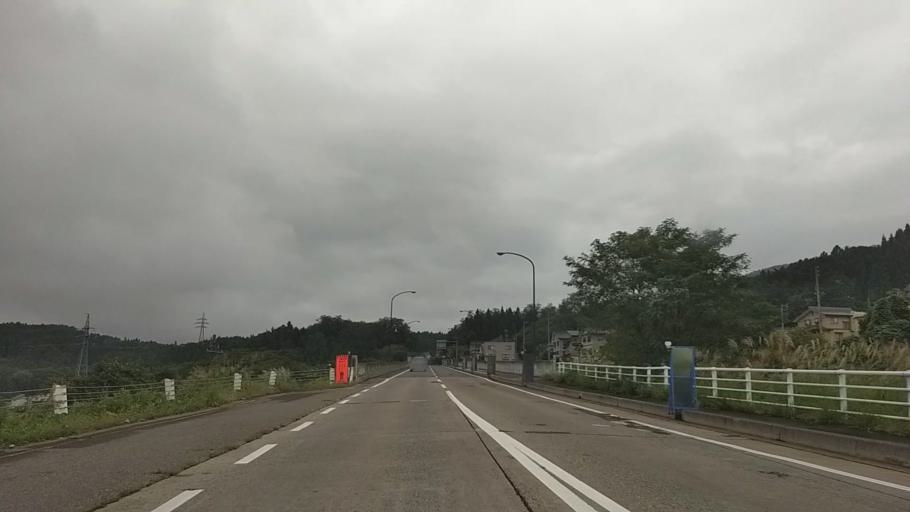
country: JP
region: Nagano
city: Iiyama
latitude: 36.8225
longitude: 138.3495
